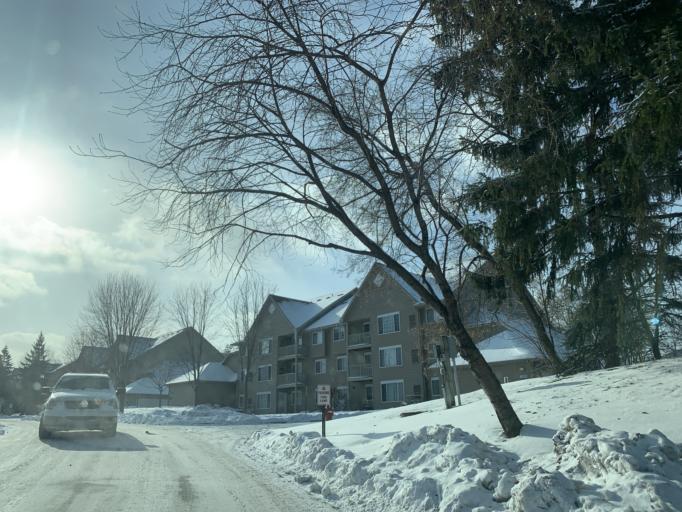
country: US
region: Minnesota
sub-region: Dakota County
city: Inver Grove Heights
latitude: 44.8737
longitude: -93.0662
